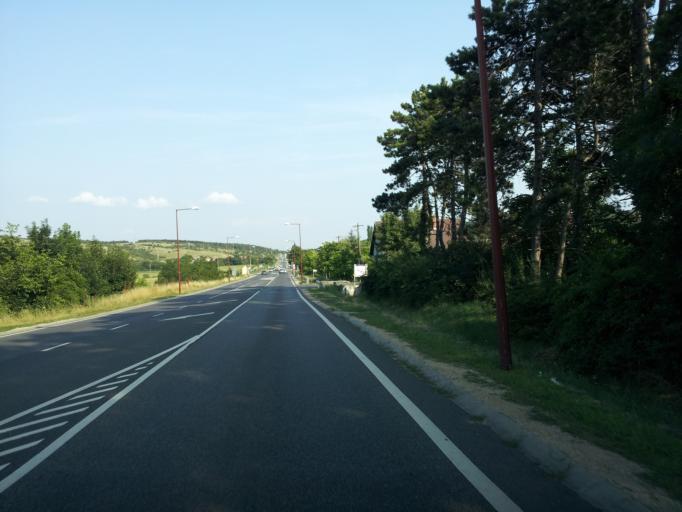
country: HU
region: Veszprem
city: Liter
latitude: 47.1028
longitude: 18.0082
